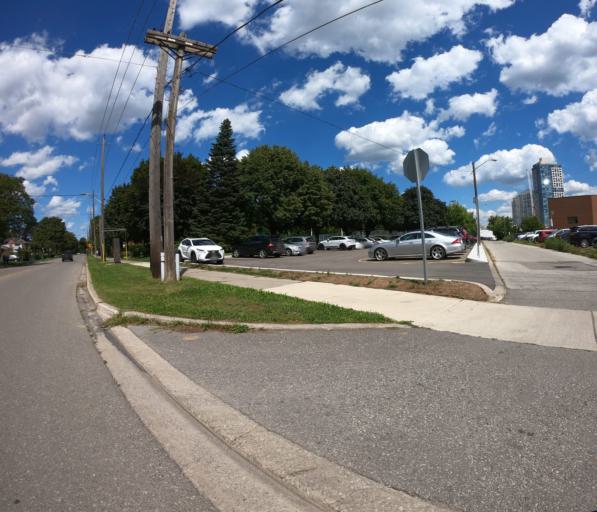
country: CA
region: Ontario
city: Etobicoke
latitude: 43.6329
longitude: -79.5454
